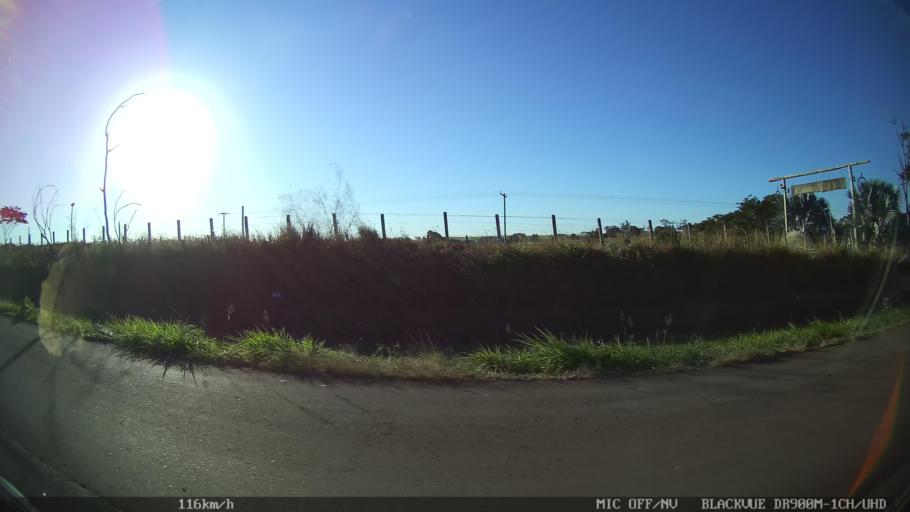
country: BR
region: Sao Paulo
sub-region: Guapiacu
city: Guapiacu
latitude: -20.7879
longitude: -49.2859
